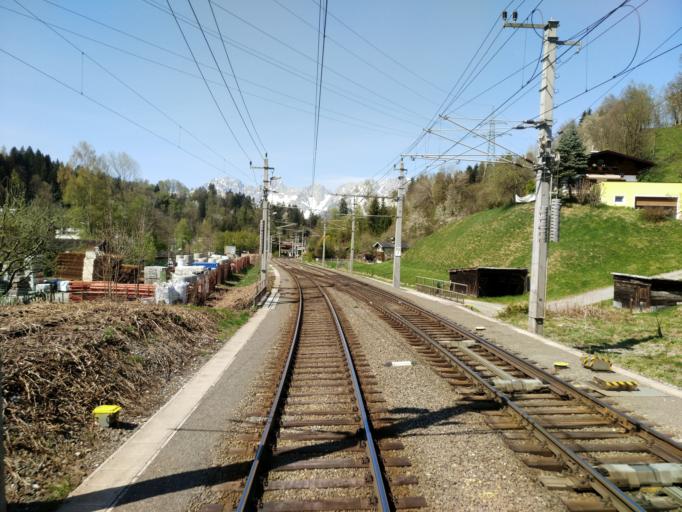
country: AT
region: Tyrol
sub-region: Politischer Bezirk Kitzbuhel
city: Kitzbuhel
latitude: 47.4573
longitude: 12.3900
